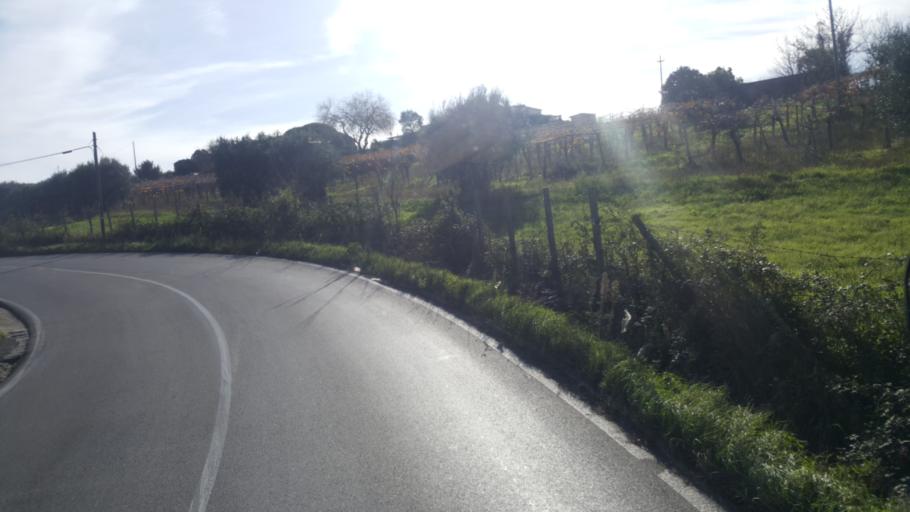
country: IT
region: Latium
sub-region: Citta metropolitana di Roma Capitale
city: Mantiglia di Ardea
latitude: 41.6777
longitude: 12.6259
